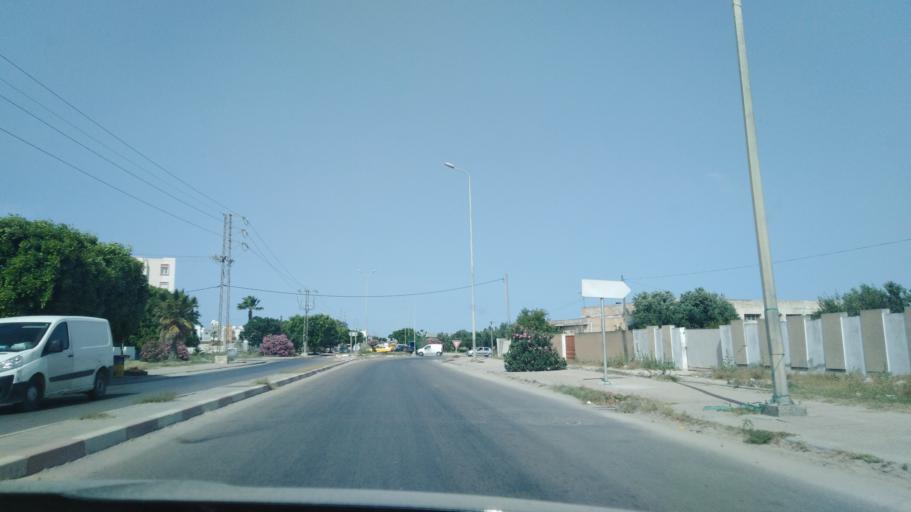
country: TN
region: Susah
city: Sousse
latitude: 35.7927
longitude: 10.5949
